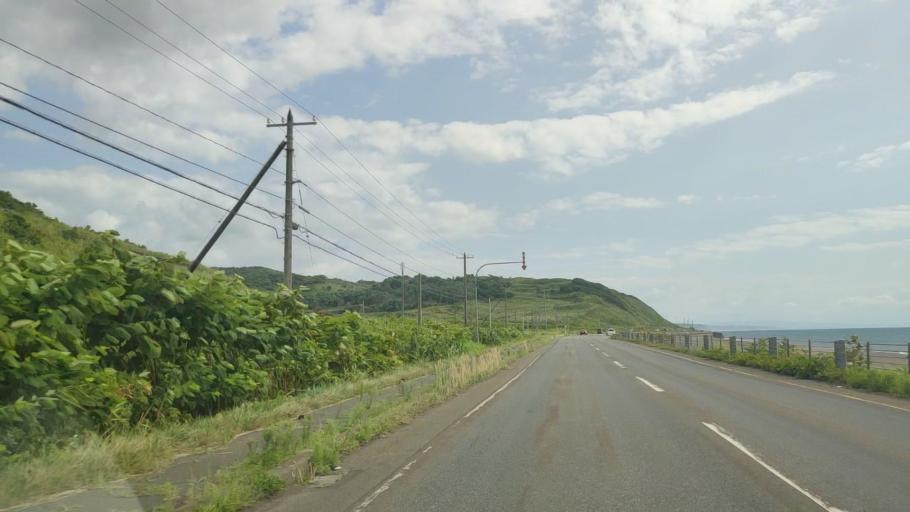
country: JP
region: Hokkaido
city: Rumoi
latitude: 44.1040
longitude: 141.6601
